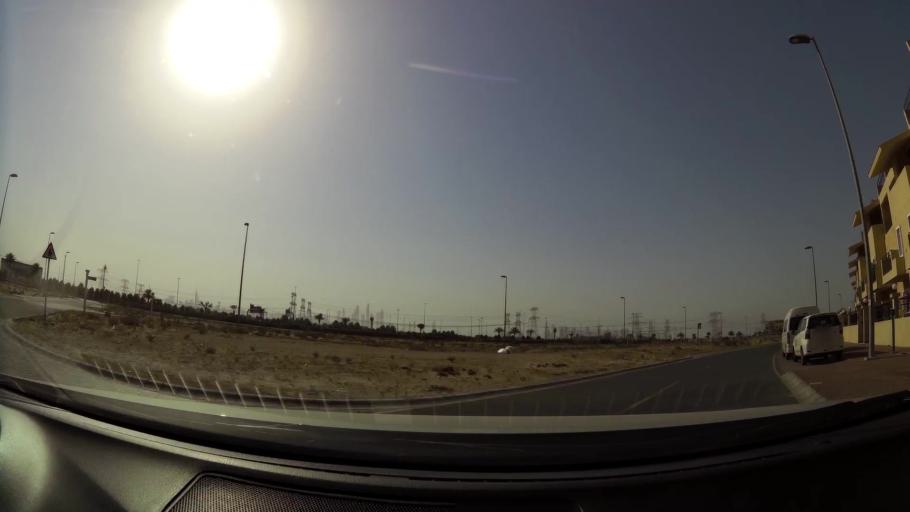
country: AE
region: Dubai
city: Dubai
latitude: 25.0553
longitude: 55.1980
